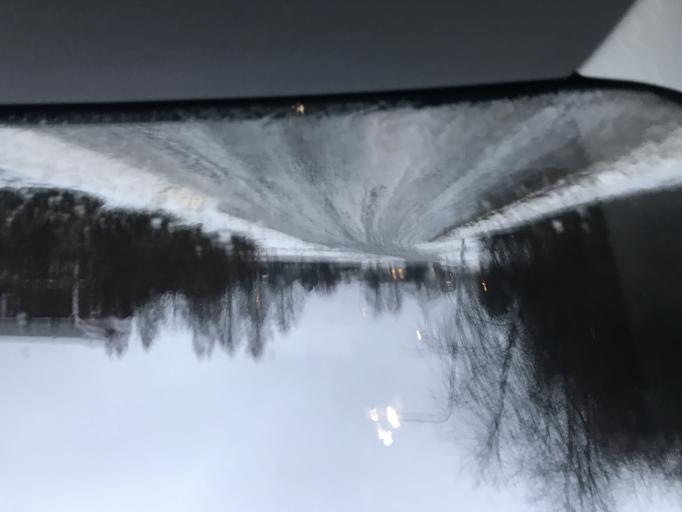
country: SE
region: Norrbotten
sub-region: Lulea Kommun
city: Sodra Sunderbyn
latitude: 65.6503
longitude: 21.9627
